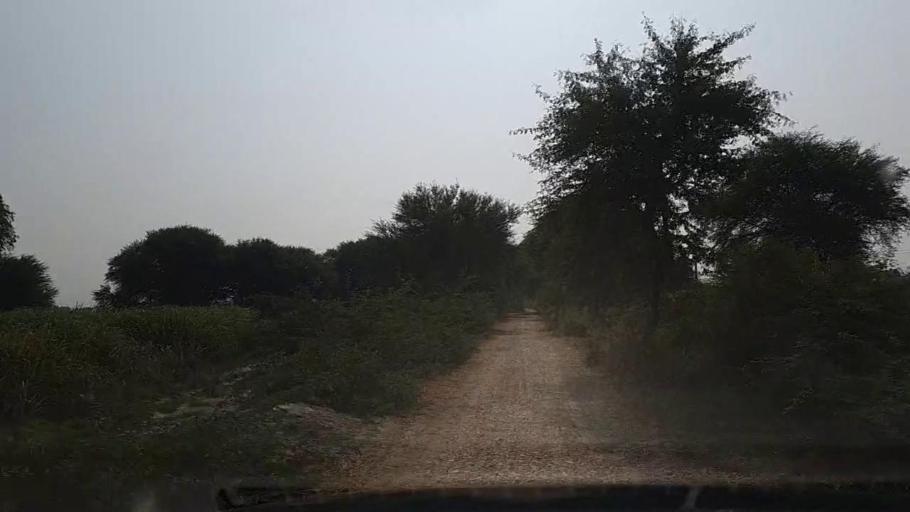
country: PK
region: Sindh
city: Mirpur Batoro
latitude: 24.6870
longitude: 68.2216
